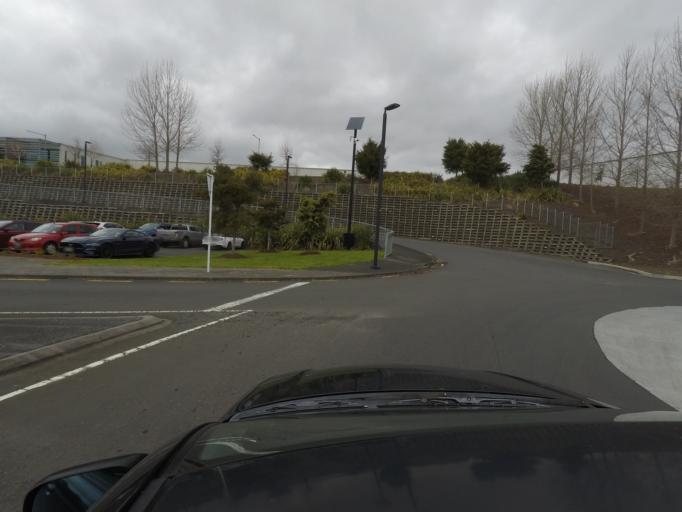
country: NZ
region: Auckland
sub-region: Auckland
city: Tamaki
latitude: -36.9399
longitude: 174.8685
